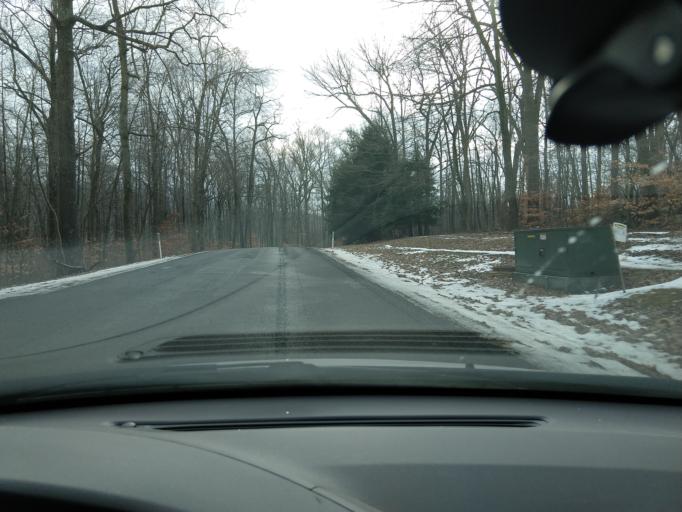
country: US
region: Pennsylvania
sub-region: Berks County
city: Birdsboro
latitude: 40.2038
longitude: -75.7908
